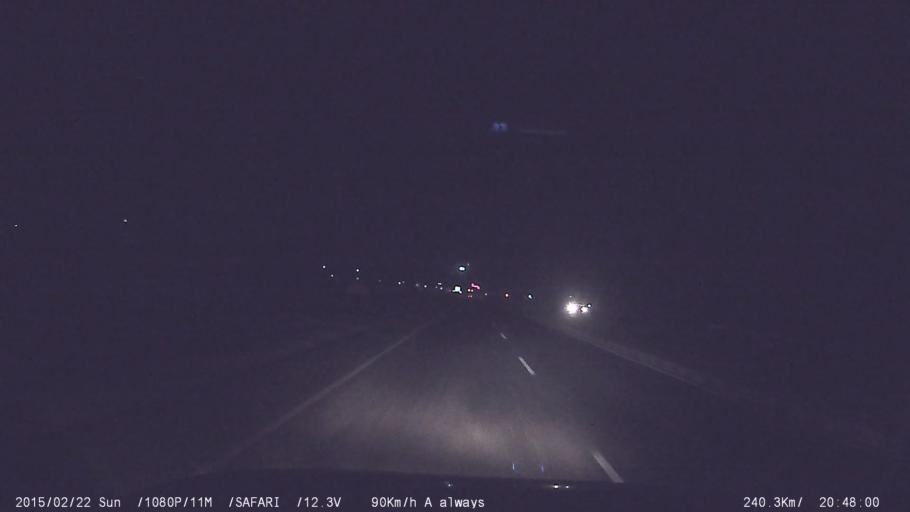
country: IN
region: Tamil Nadu
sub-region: Dindigul
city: Vedasandur
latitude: 10.5024
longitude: 77.9439
